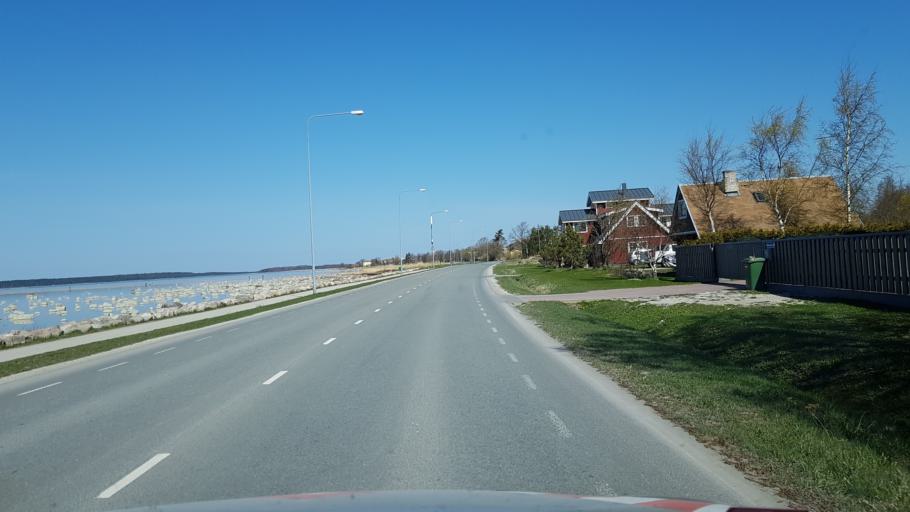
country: EE
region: Harju
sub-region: Viimsi vald
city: Rummu
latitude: 59.5461
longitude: 24.7945
